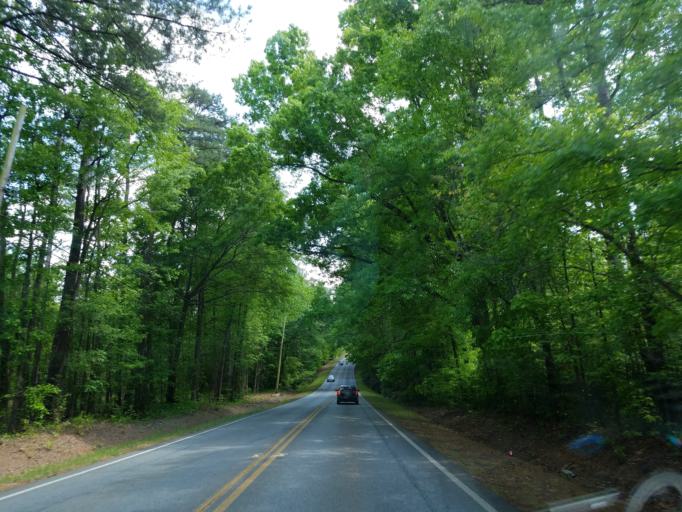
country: US
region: Georgia
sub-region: Monroe County
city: Forsyth
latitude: 33.0665
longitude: -83.9539
